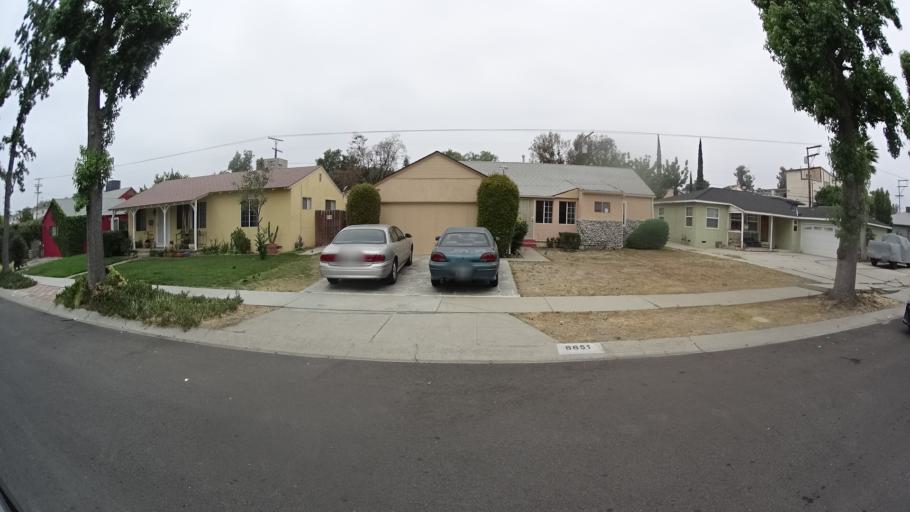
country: US
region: California
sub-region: Los Angeles County
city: Van Nuys
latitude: 34.1918
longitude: -118.4128
